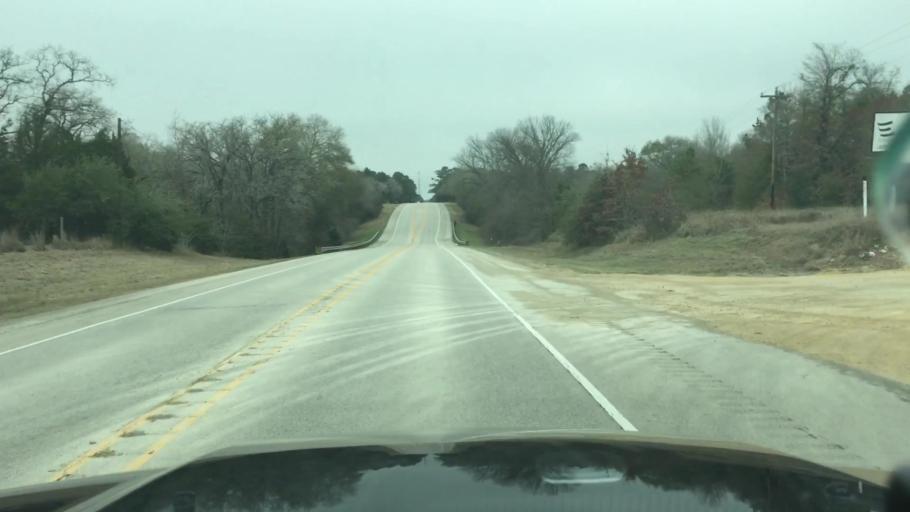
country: US
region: Texas
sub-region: Fayette County
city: La Grange
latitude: 30.0033
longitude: -96.8929
